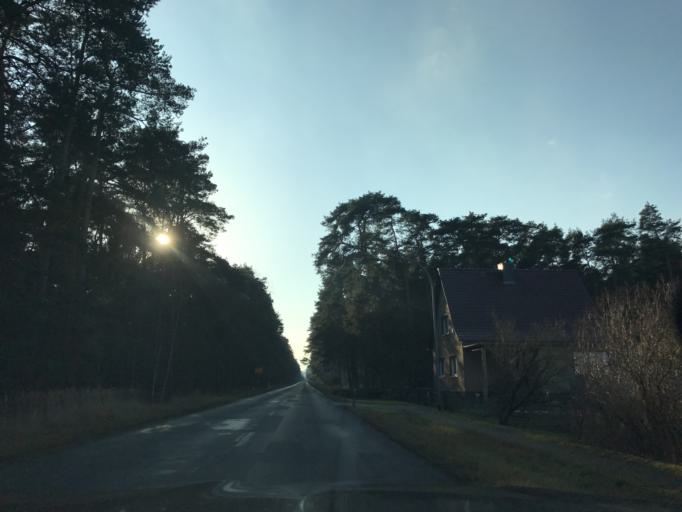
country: DE
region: Brandenburg
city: Wenzlow
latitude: 52.2923
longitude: 12.4516
